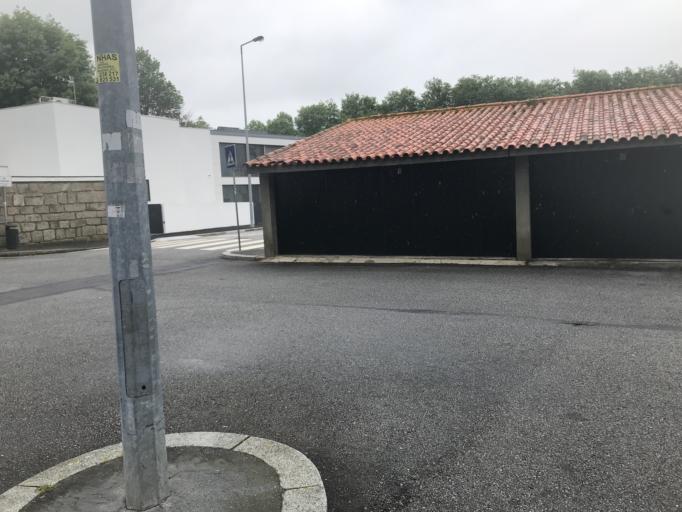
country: PT
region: Porto
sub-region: Matosinhos
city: Senhora da Hora
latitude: 41.1782
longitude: -8.6609
